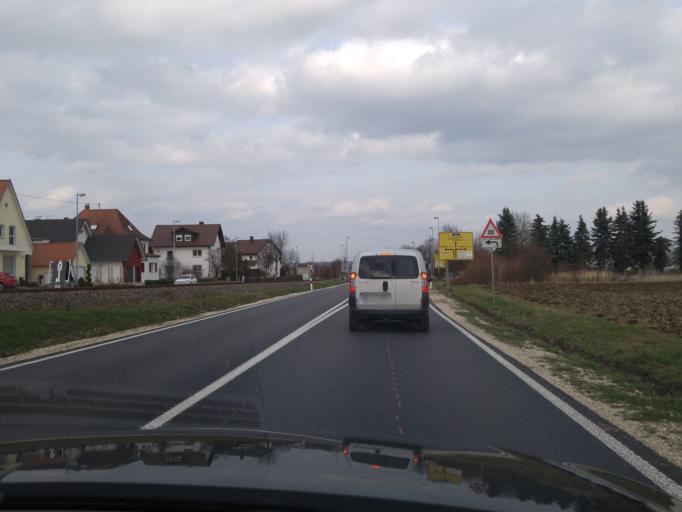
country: DE
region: Baden-Wuerttemberg
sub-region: Regierungsbezirk Stuttgart
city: Dettingen unter Teck
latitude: 48.6115
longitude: 9.4542
